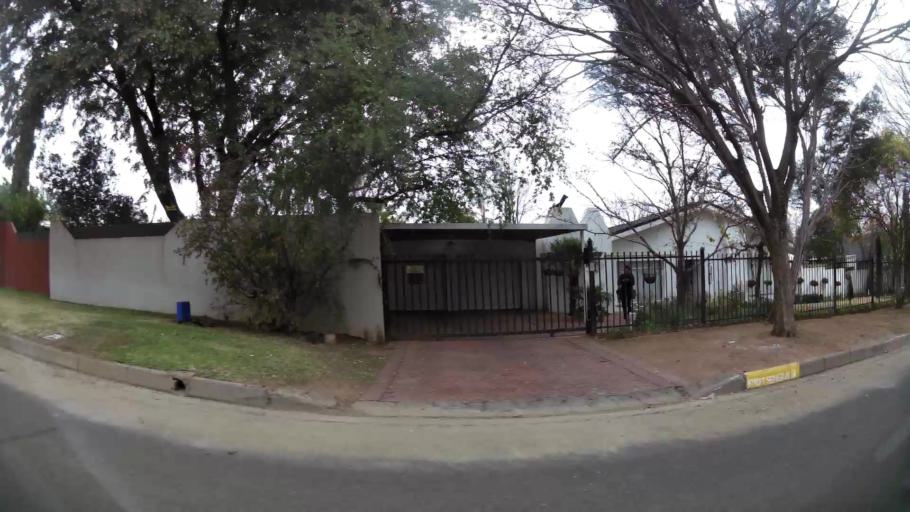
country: ZA
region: Orange Free State
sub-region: Mangaung Metropolitan Municipality
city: Bloemfontein
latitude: -29.0916
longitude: 26.2140
